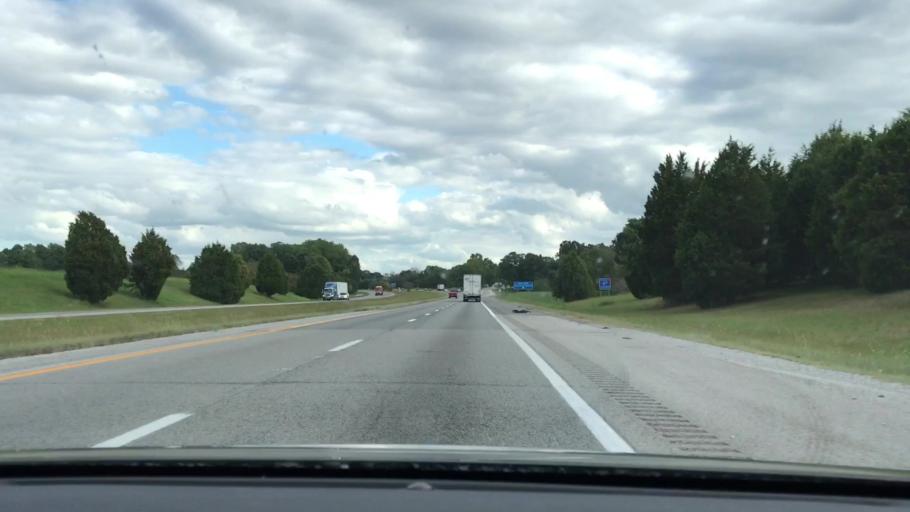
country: US
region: Kentucky
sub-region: Christian County
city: Oak Grove
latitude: 36.6417
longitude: -87.3398
